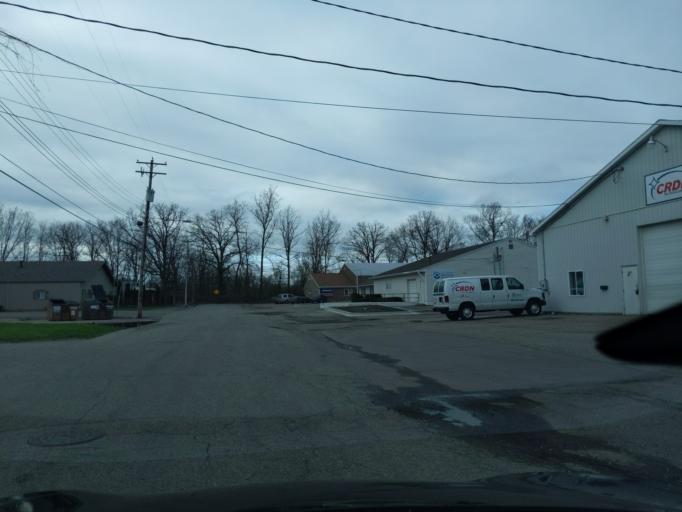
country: US
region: Michigan
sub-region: Ingham County
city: Edgemont Park
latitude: 42.7292
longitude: -84.5919
